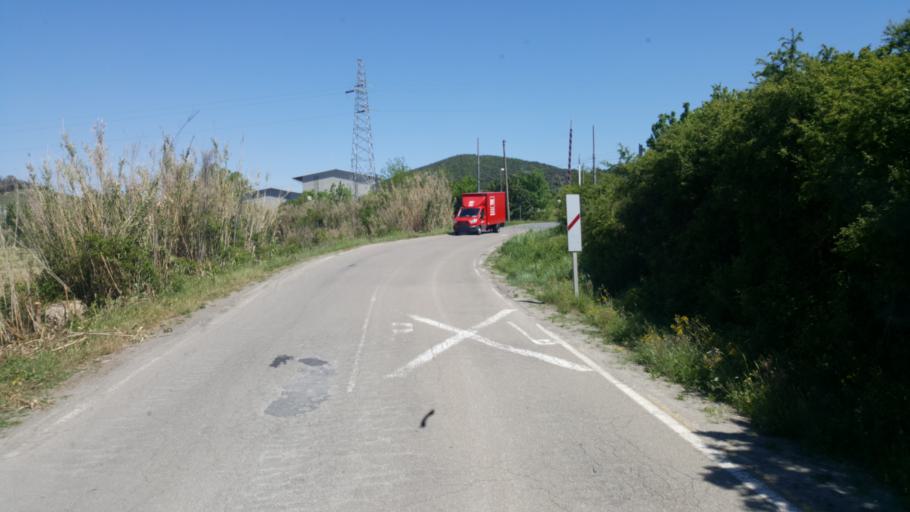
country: IT
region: Tuscany
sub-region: Provincia di Livorno
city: Rosignano Marittimo
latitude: 43.4072
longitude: 10.4950
